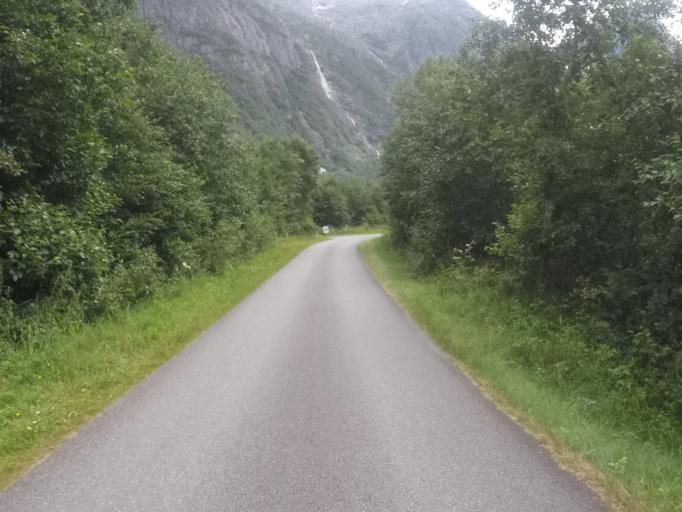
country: NO
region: Sogn og Fjordane
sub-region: Stryn
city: Stryn
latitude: 61.7750
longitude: 7.0212
